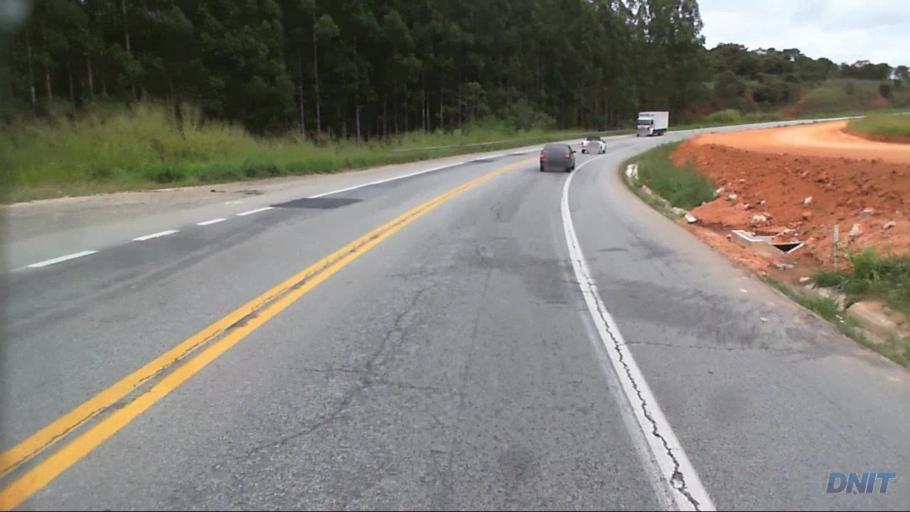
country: BR
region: Minas Gerais
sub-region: Barao De Cocais
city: Barao de Cocais
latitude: -19.7670
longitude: -43.4579
